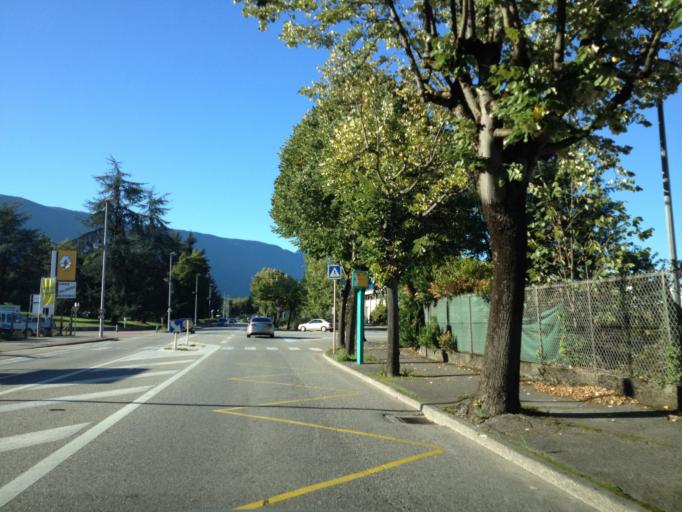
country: FR
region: Rhone-Alpes
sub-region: Departement de la Savoie
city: La Motte-Servolex
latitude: 45.5862
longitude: 5.8842
